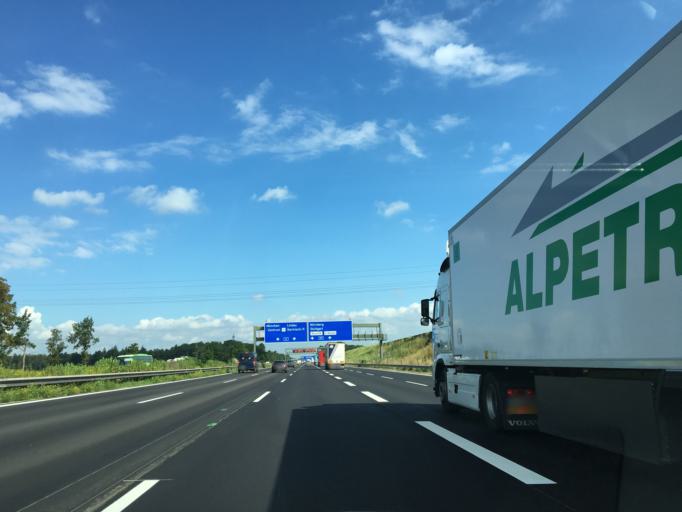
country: DE
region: Bavaria
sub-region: Upper Bavaria
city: Brunnthal
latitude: 47.9988
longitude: 11.6758
